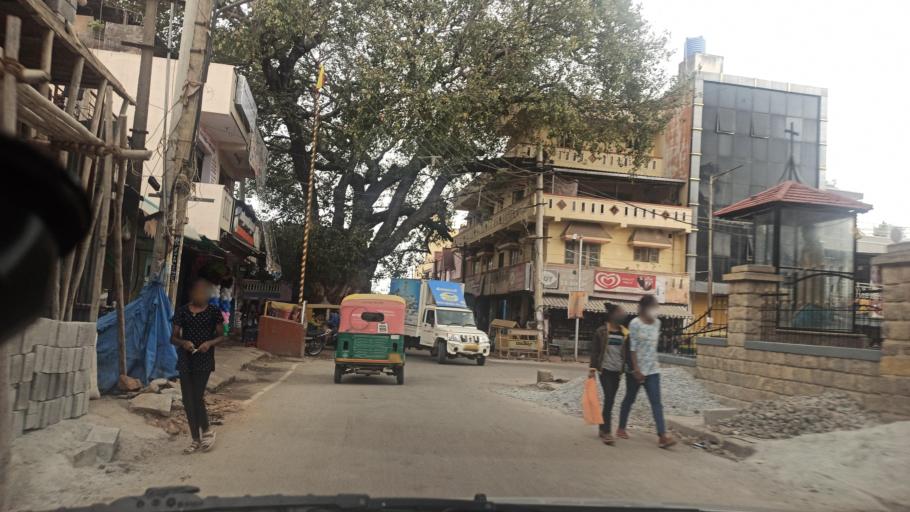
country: IN
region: Karnataka
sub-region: Bangalore Urban
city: Yelahanka
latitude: 13.0391
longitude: 77.6050
